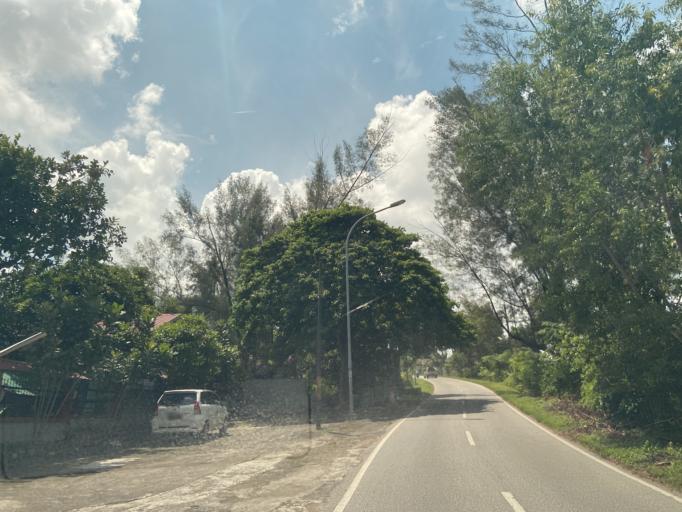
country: SG
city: Singapore
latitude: 1.1534
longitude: 104.0085
